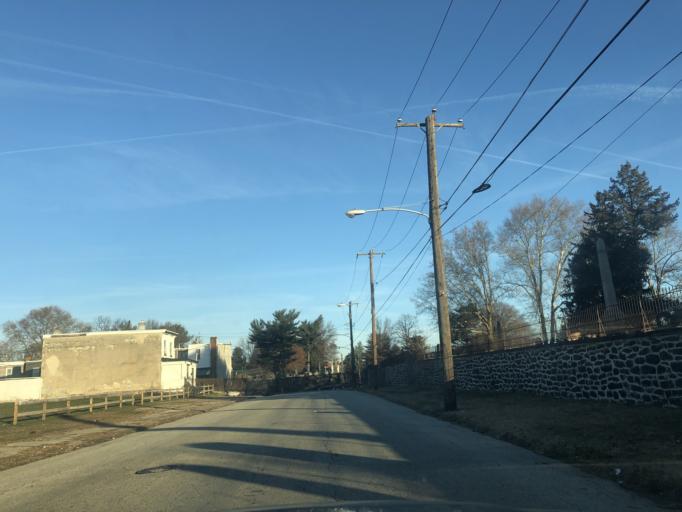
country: US
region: Pennsylvania
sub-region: Delaware County
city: Millbourne
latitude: 39.9688
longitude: -75.2229
